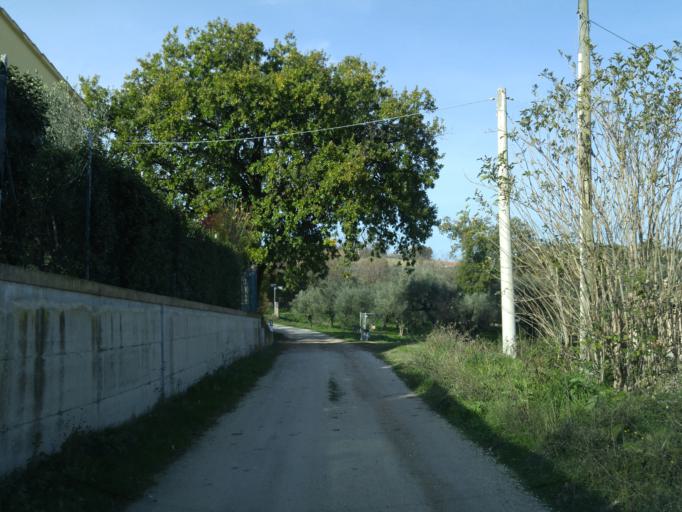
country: IT
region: The Marches
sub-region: Provincia di Pesaro e Urbino
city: Saltara
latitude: 43.7603
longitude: 12.9012
